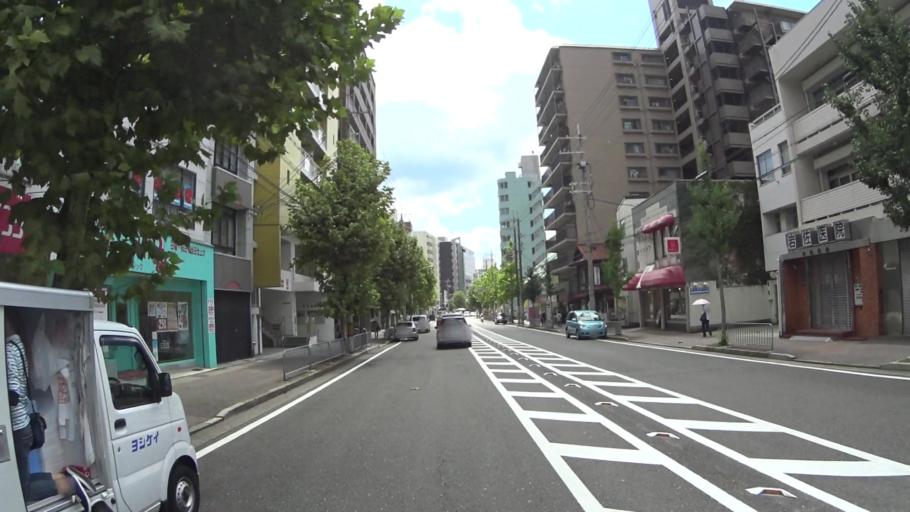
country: JP
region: Shiga Prefecture
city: Otsu-shi
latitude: 34.9885
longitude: 135.8173
